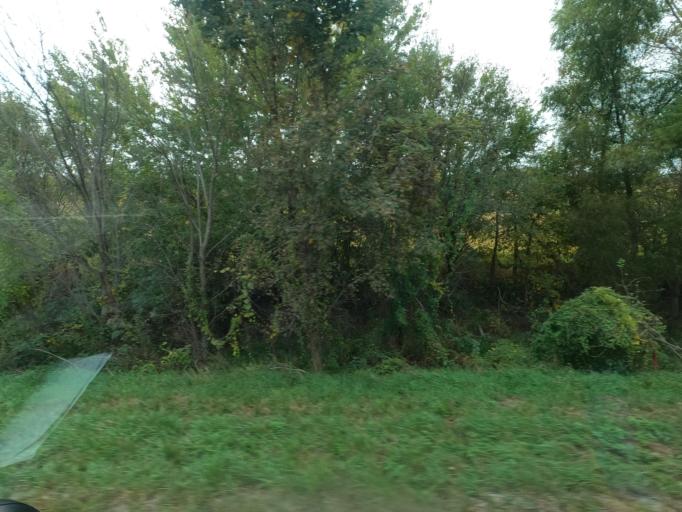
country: US
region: Iowa
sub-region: Jefferson County
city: Fairfield
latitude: 40.8772
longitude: -92.1564
